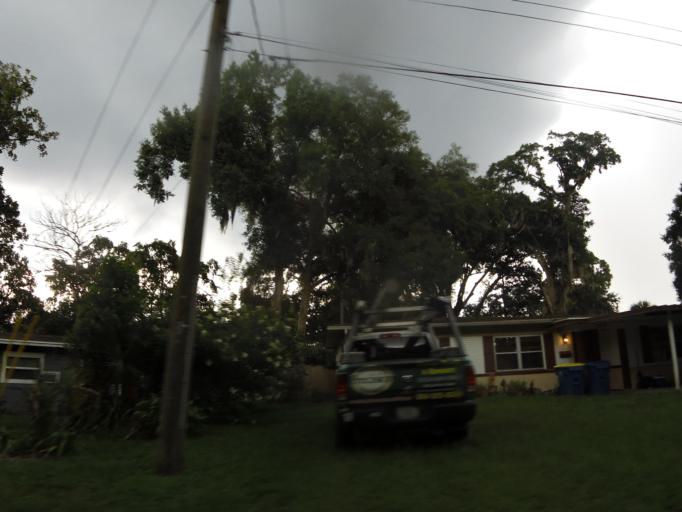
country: US
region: Florida
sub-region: Duval County
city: Jacksonville
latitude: 30.3425
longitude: -81.6052
